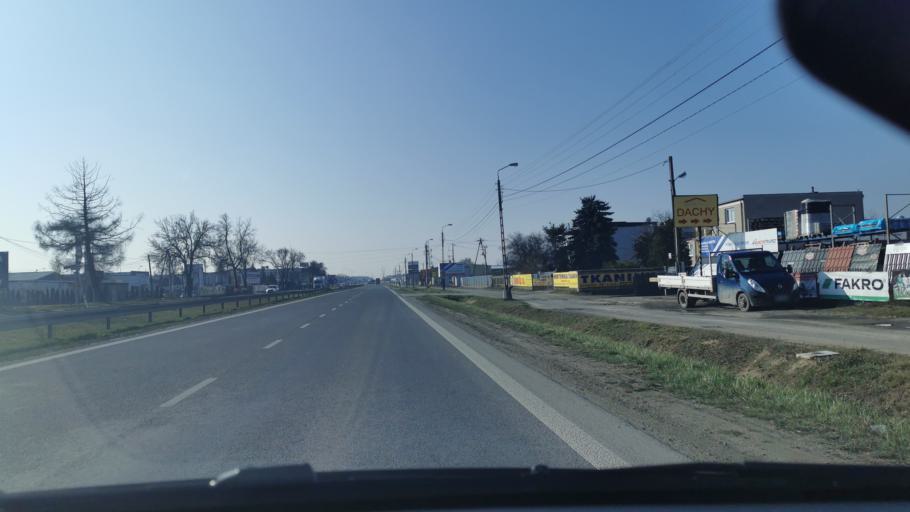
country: PL
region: Masovian Voivodeship
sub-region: Powiat pruszkowski
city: Nowe Grocholice
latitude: 52.1194
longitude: 20.8928
